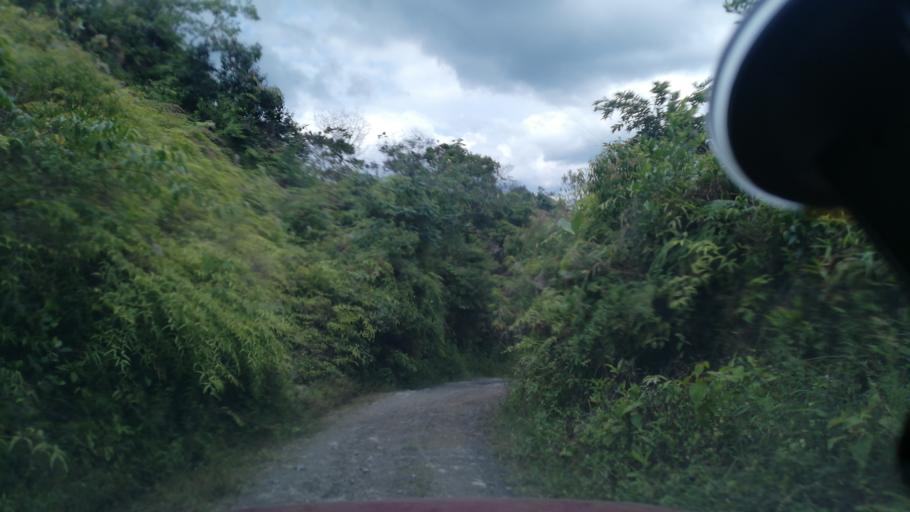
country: CO
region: Cundinamarca
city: Vergara
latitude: 5.1988
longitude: -74.2917
